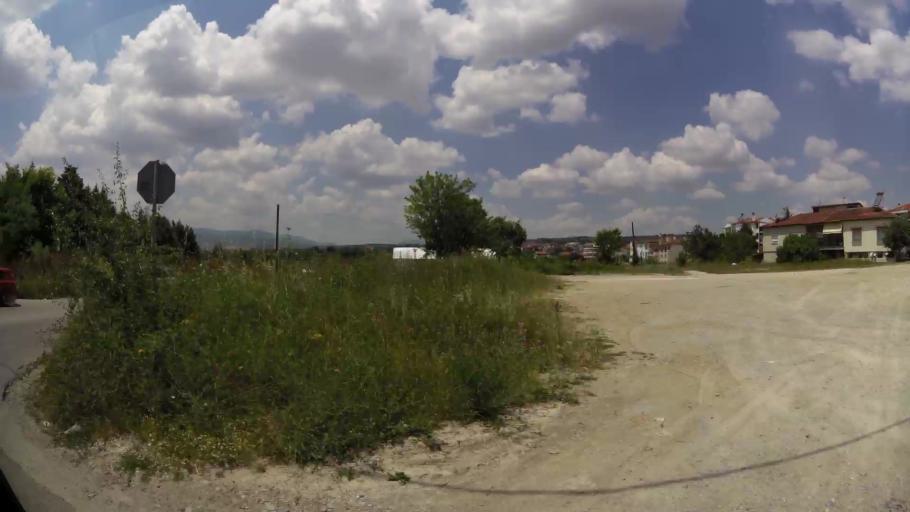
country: GR
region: West Macedonia
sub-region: Nomos Kozanis
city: Kozani
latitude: 40.2888
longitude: 21.7981
